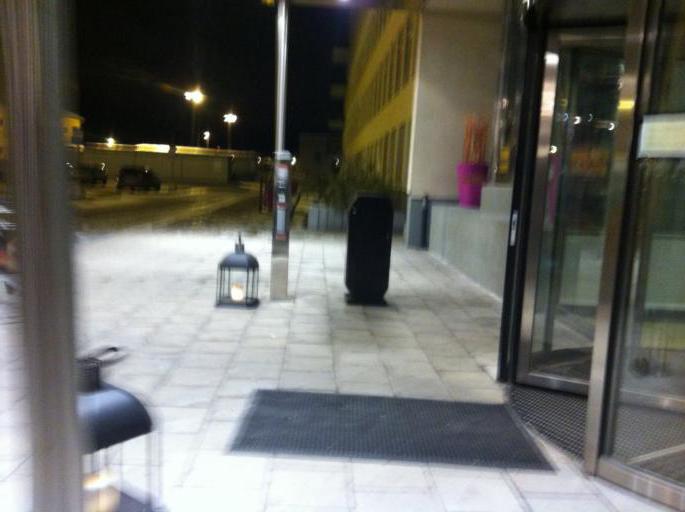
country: SE
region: Stockholm
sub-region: Stockholms Kommun
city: Bromma
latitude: 59.3578
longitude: 17.9478
